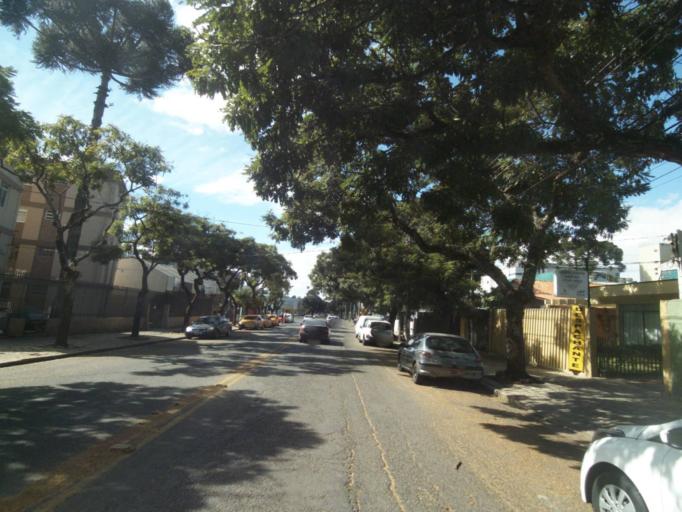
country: BR
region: Parana
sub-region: Curitiba
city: Curitiba
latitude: -25.4659
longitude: -49.2853
